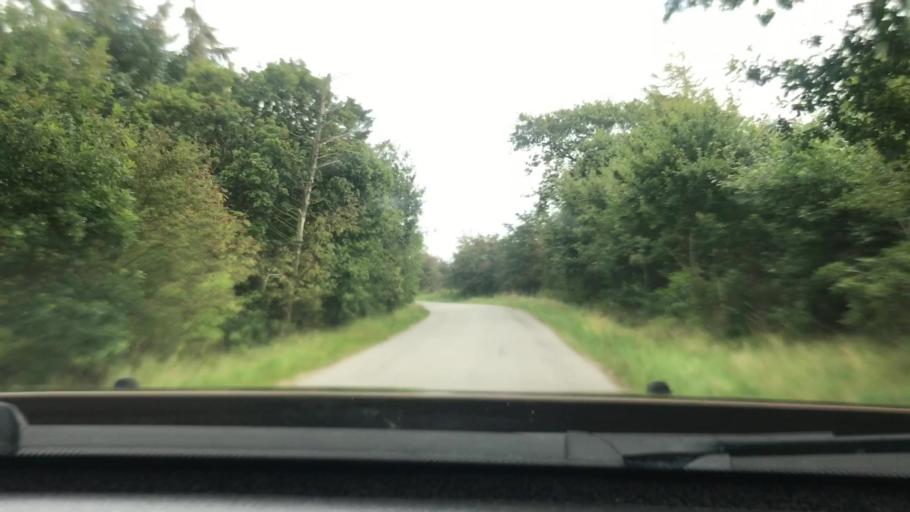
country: DK
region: South Denmark
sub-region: Esbjerg Kommune
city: Ribe
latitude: 55.2989
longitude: 8.7274
